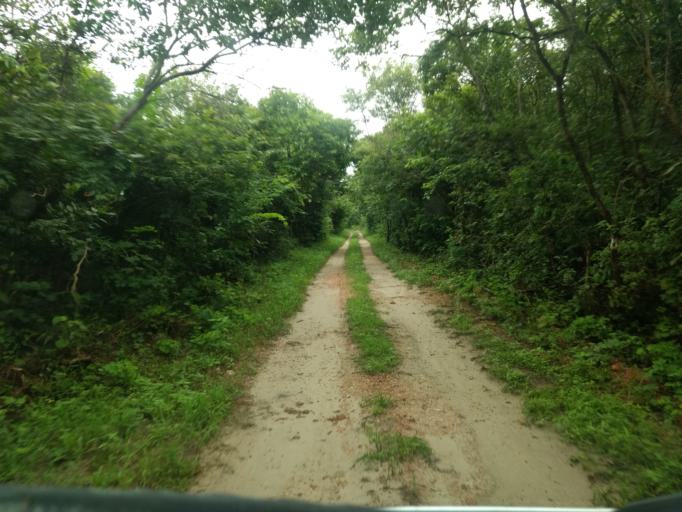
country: BR
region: Ceara
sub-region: Crateus
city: Crateus
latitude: -5.1490
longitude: -40.9189
